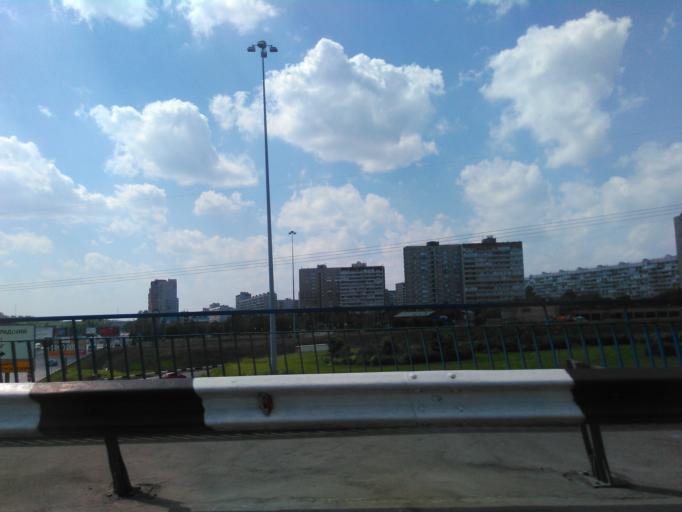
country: RU
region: Moscow
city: Ivanovskoye
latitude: 55.7773
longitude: 37.8423
